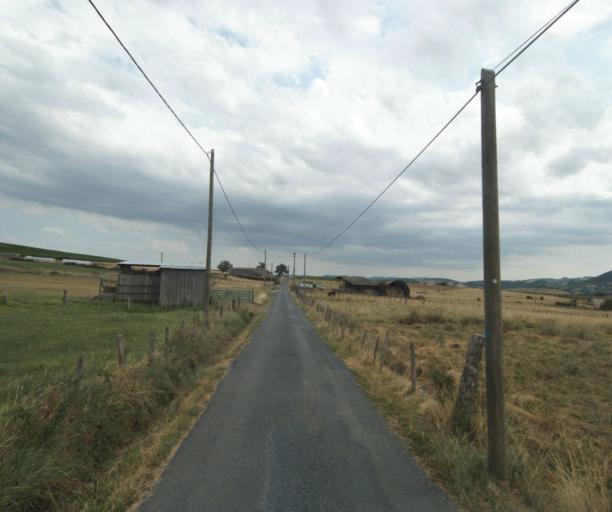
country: FR
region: Rhone-Alpes
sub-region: Departement du Rhone
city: Bully
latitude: 45.8760
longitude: 4.5562
